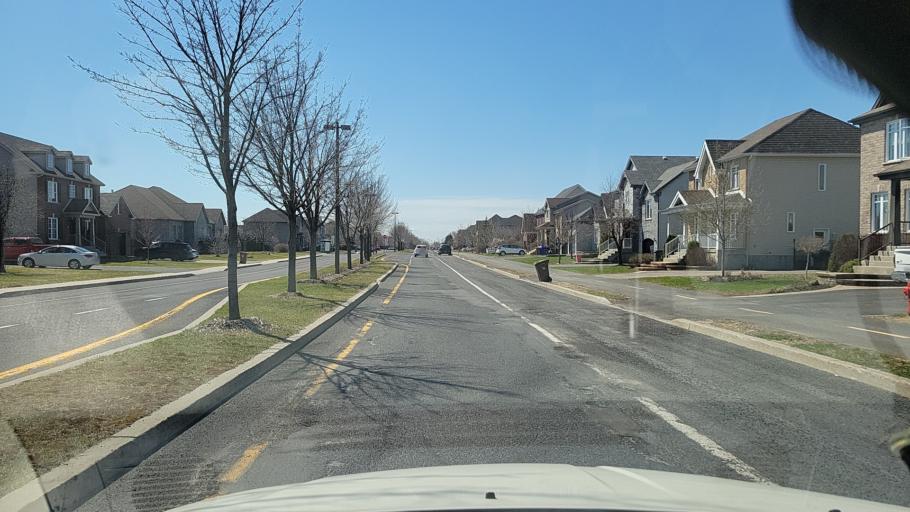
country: CA
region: Quebec
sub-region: Monteregie
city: Sainte-Julie
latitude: 45.5833
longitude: -73.3540
